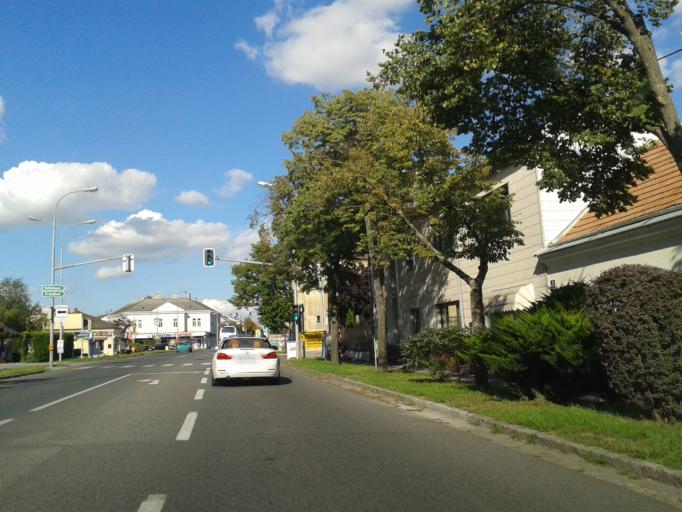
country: AT
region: Lower Austria
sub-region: Politischer Bezirk Ganserndorf
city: Deutsch-Wagram
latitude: 48.2984
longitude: 16.5636
